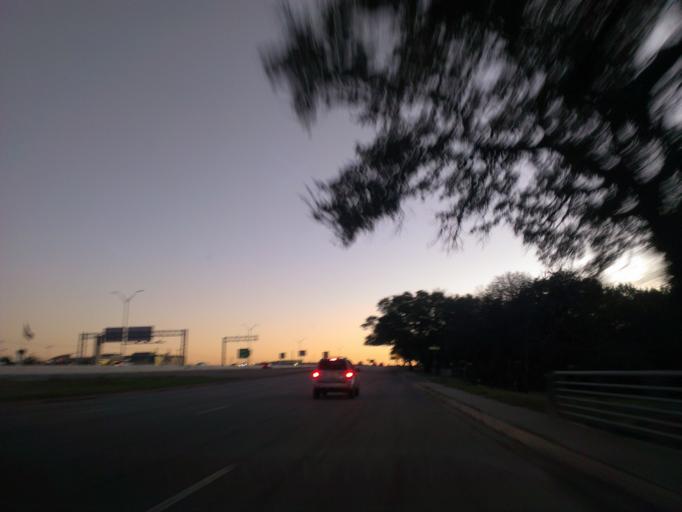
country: US
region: Texas
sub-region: Travis County
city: Wells Branch
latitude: 30.4191
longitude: -97.7053
